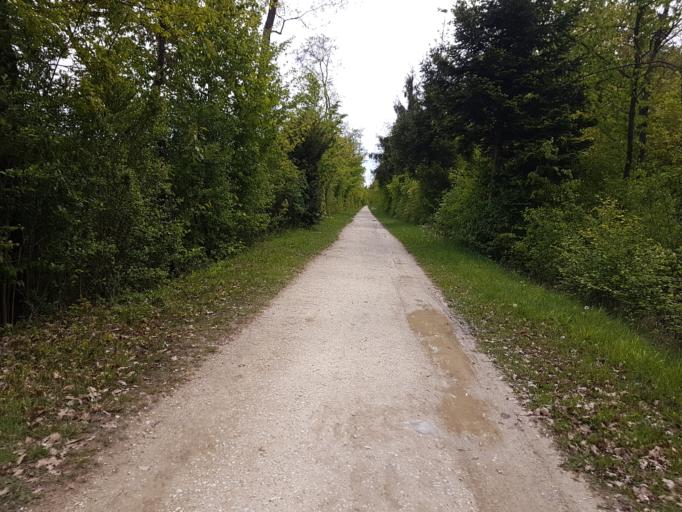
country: CH
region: Aargau
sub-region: Bezirk Brugg
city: Veltheim
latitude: 47.4320
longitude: 8.1604
